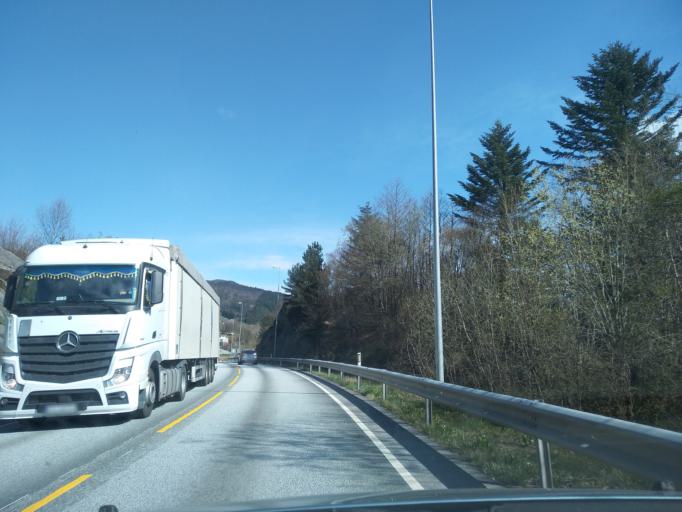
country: NO
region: Rogaland
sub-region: Tysvaer
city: Aksdal
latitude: 59.5027
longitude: 5.5852
